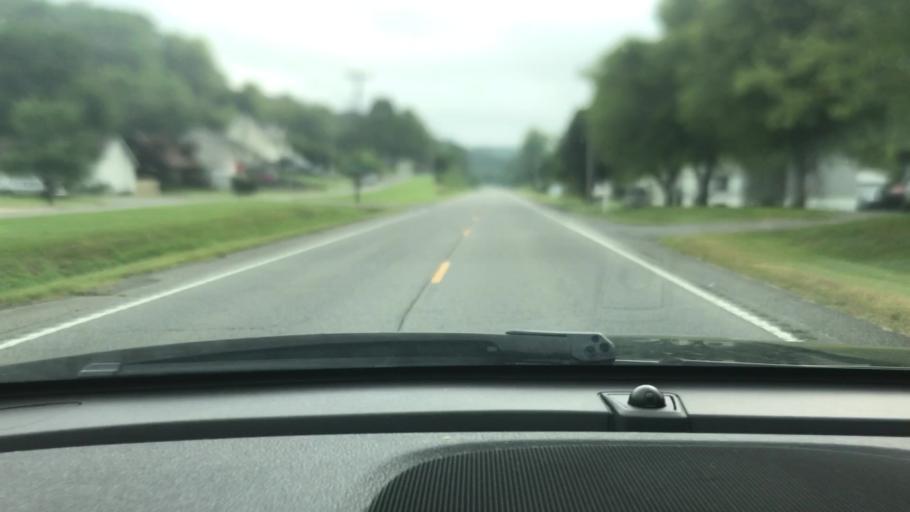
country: US
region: Tennessee
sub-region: Sumner County
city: Millersville
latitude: 36.3898
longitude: -86.6938
